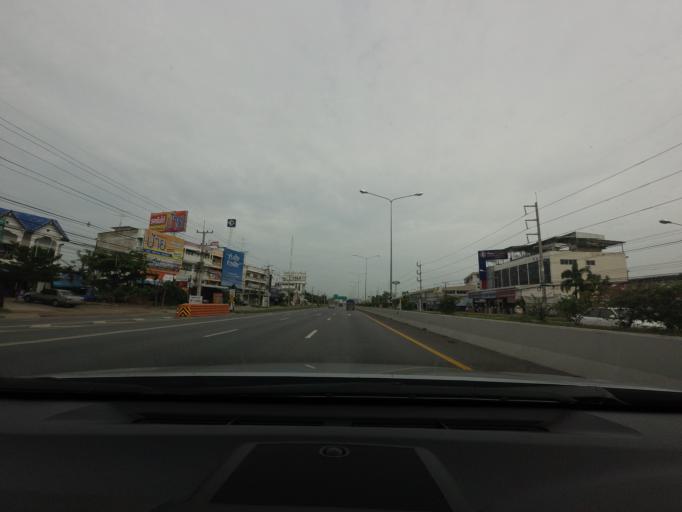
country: TH
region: Phetchaburi
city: Phetchaburi
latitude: 13.0968
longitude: 99.9385
